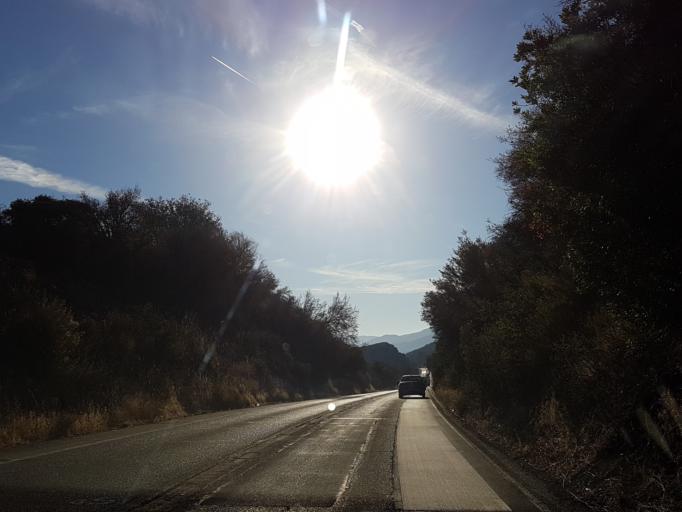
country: US
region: California
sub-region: Santa Barbara County
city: Santa Ynez
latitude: 34.5674
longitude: -119.9422
